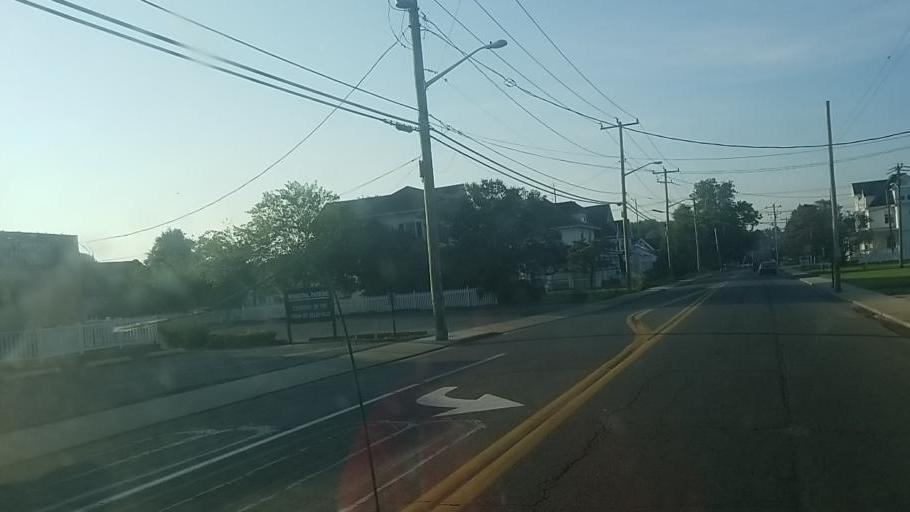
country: US
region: Delaware
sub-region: Sussex County
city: Selbyville
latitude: 38.4603
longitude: -75.2212
